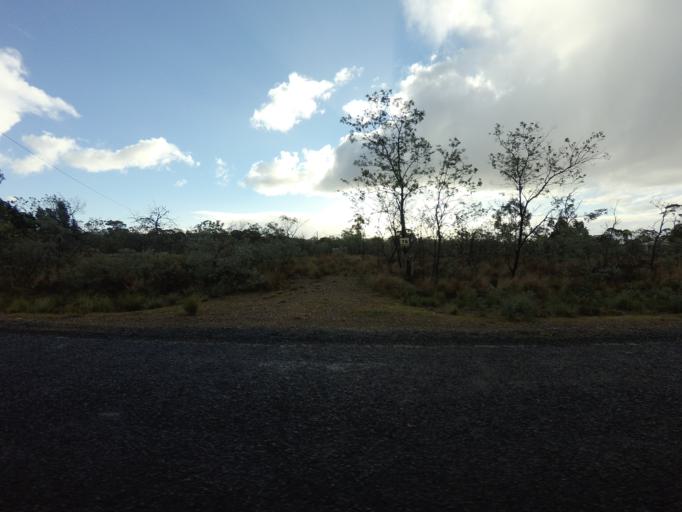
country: AU
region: Tasmania
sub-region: Break O'Day
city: St Helens
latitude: -42.1044
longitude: 148.0716
